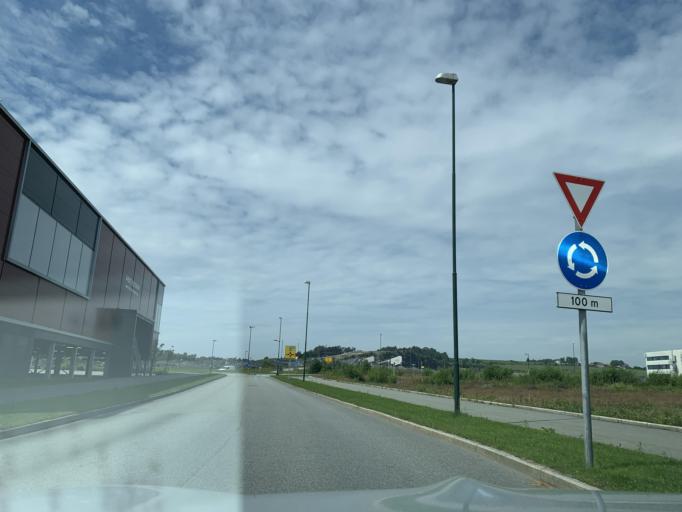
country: NO
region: Rogaland
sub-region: Sola
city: Sola
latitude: 58.8942
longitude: 5.6817
